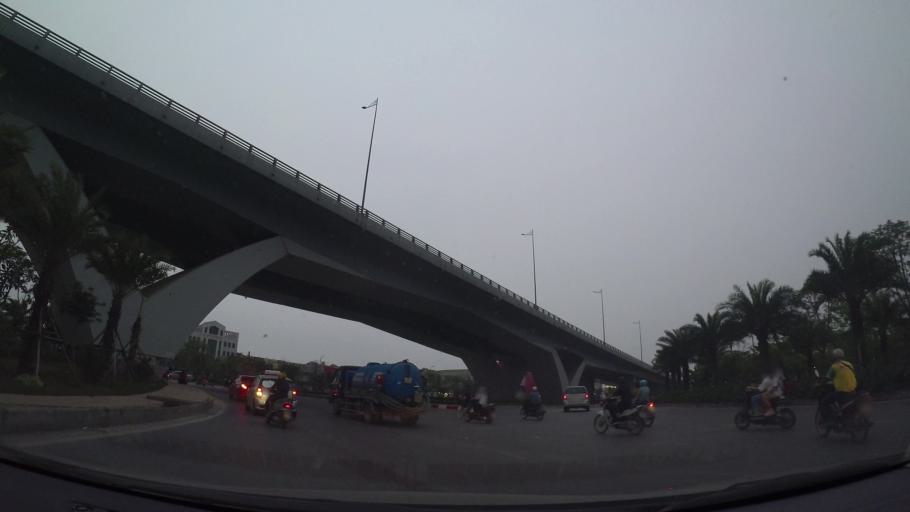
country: VN
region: Ha Noi
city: Hoan Kiem
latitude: 21.0547
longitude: 105.8882
